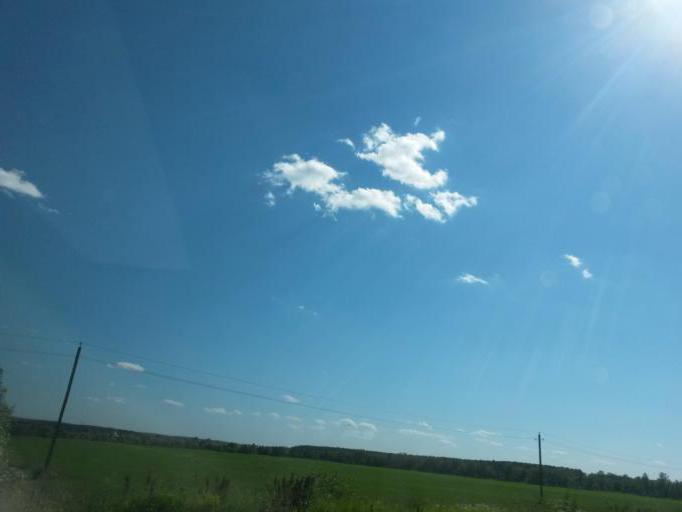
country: RU
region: Moskovskaya
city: Protvino
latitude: 54.8918
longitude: 37.3029
